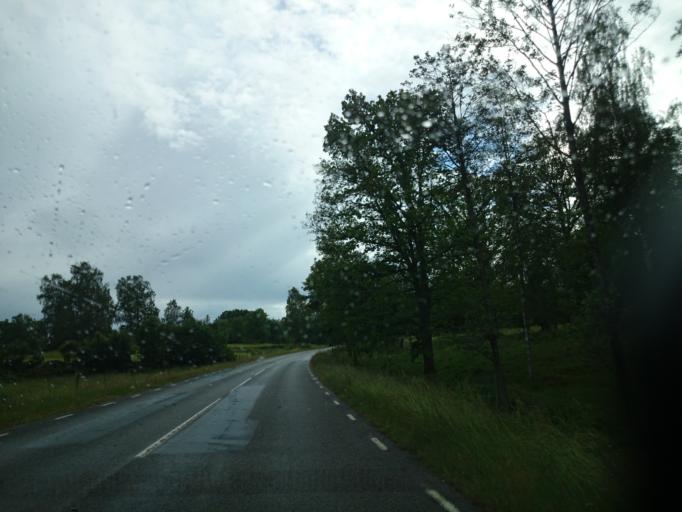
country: SE
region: Joenkoeping
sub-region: Varnamo Kommun
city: Varnamo
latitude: 57.0776
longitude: 13.9437
